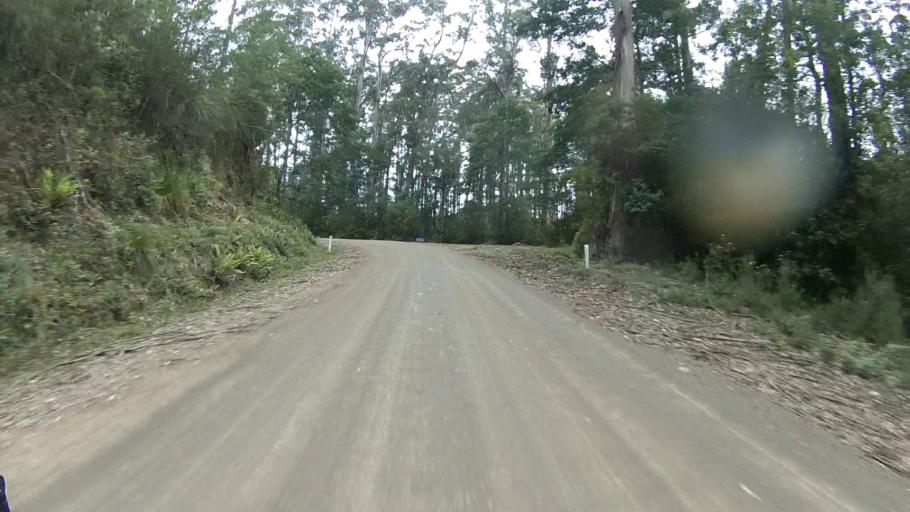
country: AU
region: Tasmania
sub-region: Sorell
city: Sorell
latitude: -42.7040
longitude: 147.8563
